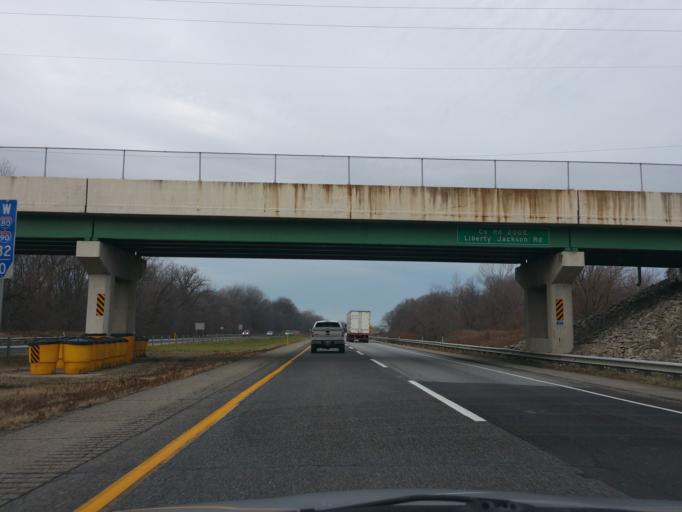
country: US
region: Indiana
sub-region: Porter County
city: Chesterton
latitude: 41.5718
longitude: -87.0276
